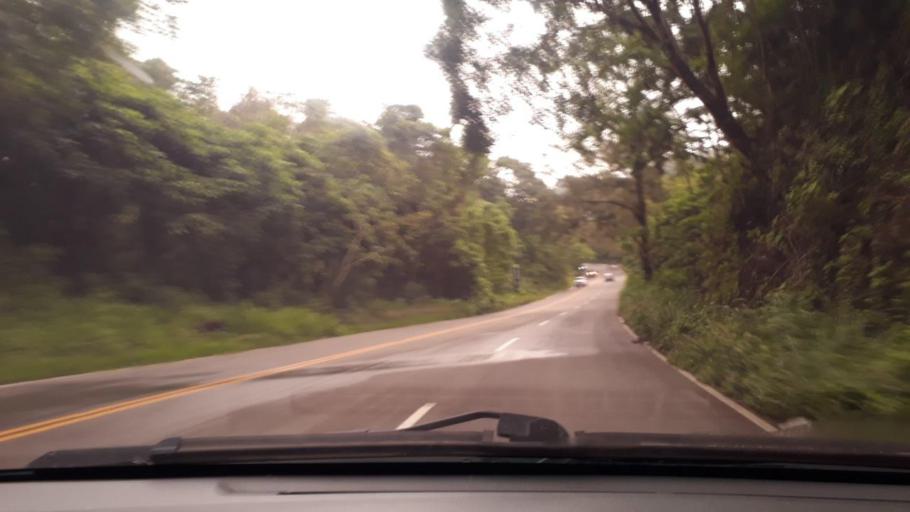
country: GT
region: Chiquimula
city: Esquipulas
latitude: 14.5522
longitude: -89.3853
